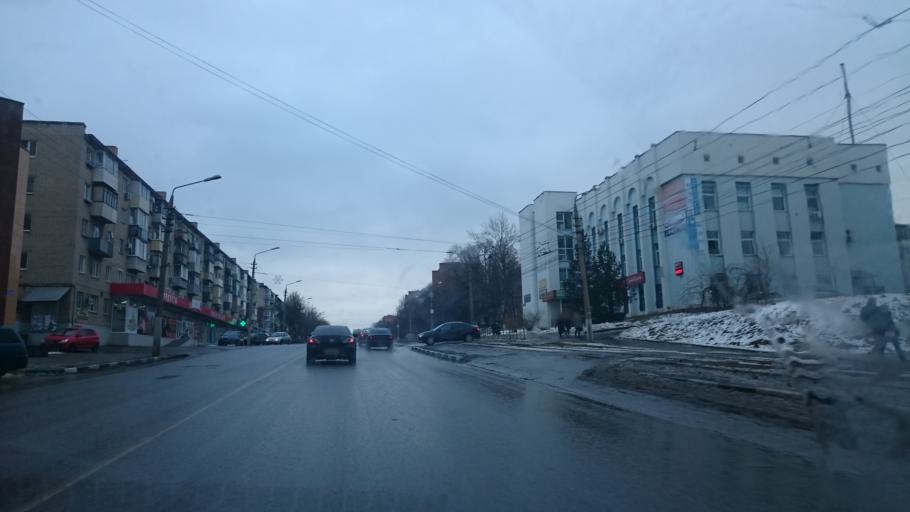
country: RU
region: Tula
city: Tula
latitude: 54.1960
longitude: 37.6669
